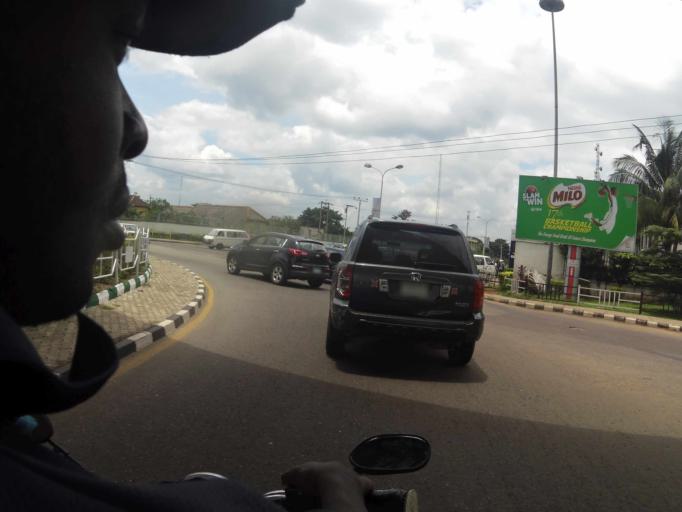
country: NG
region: Oyo
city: Ibadan
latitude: 7.4083
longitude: 3.9112
